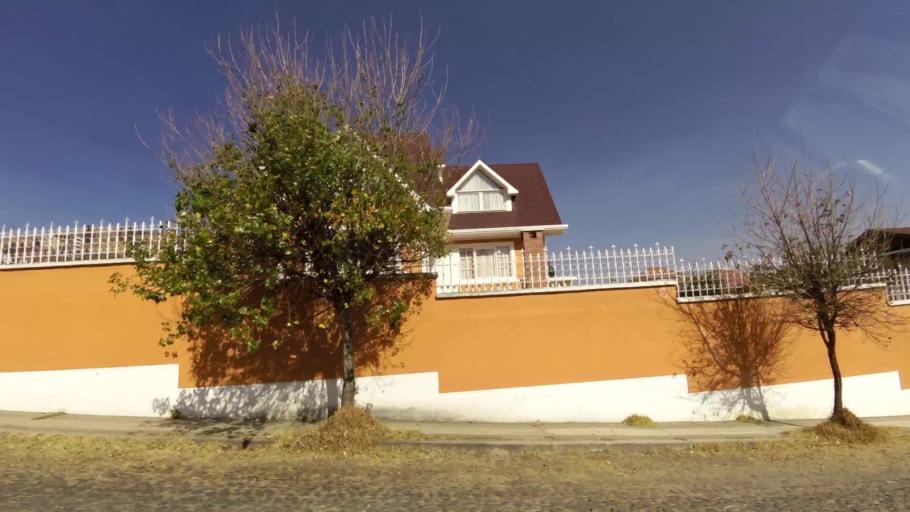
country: BO
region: La Paz
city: La Paz
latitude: -16.5102
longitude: -68.0564
